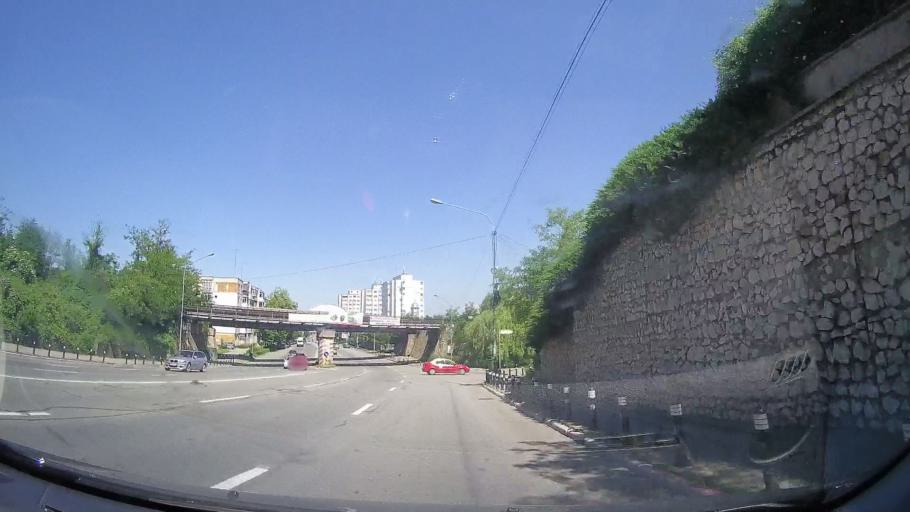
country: RO
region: Arges
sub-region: Comuna Bradu
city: Geamana
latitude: 44.8281
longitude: 24.9127
